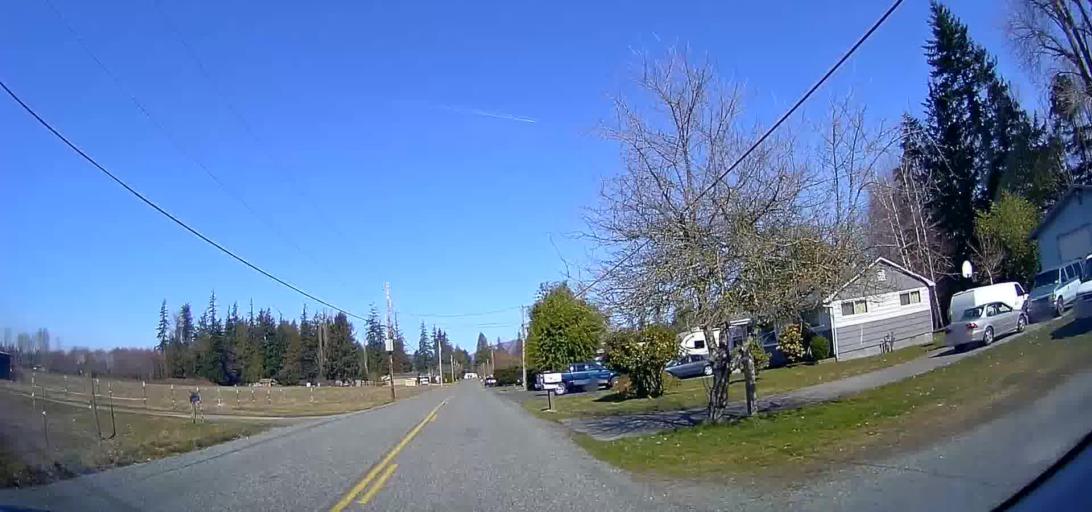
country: US
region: Washington
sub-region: Skagit County
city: Sedro-Woolley
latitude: 48.4903
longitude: -122.2749
